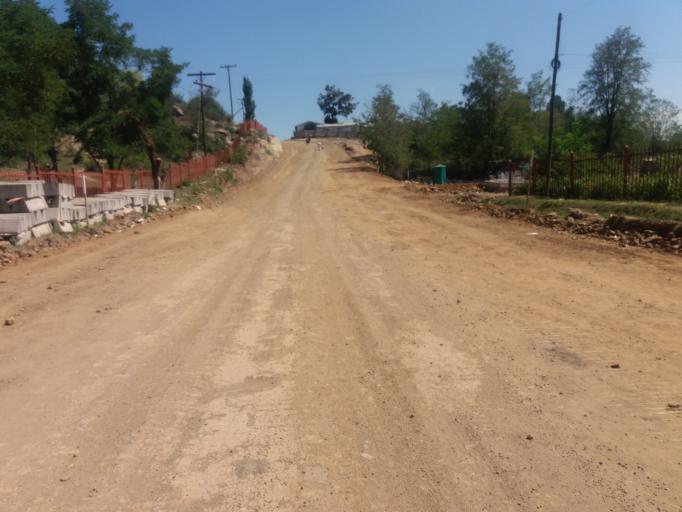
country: LS
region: Maseru
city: Maseru
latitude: -29.3187
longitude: 27.5041
